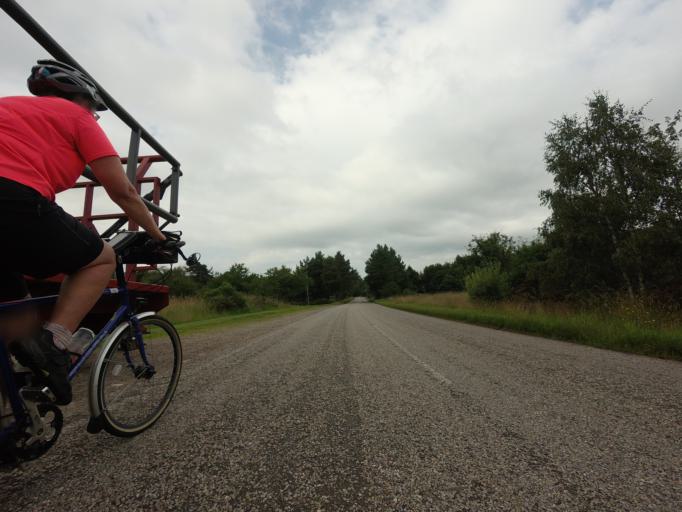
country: GB
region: Scotland
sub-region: Highland
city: Evanton
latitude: 57.9409
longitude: -4.4069
